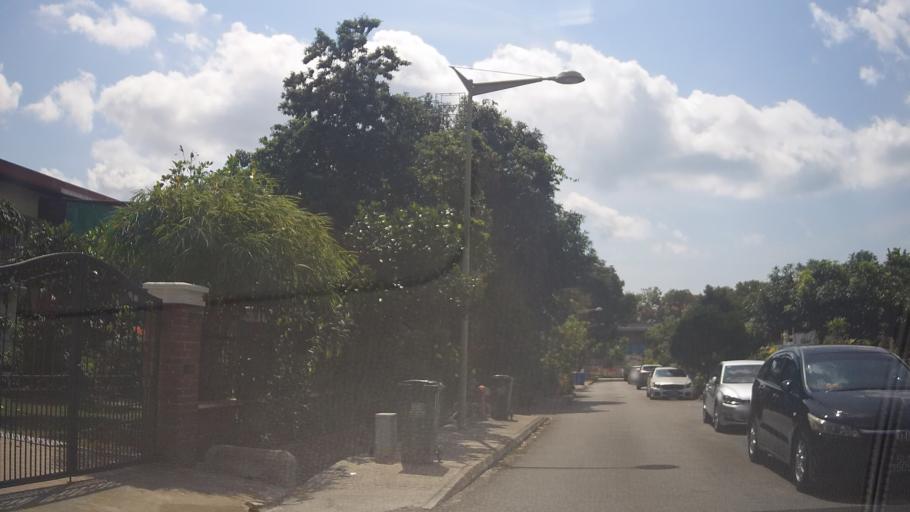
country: SG
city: Singapore
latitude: 1.3303
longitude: 103.9494
